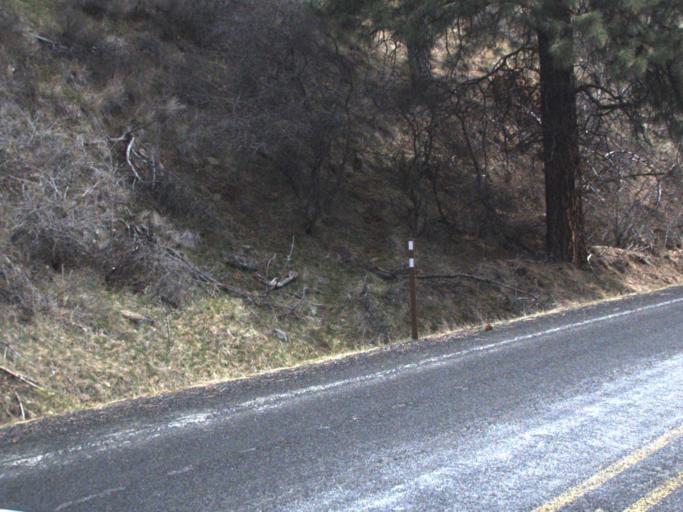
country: US
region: Washington
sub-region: Yakima County
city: Tieton
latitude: 46.8836
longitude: -120.9831
